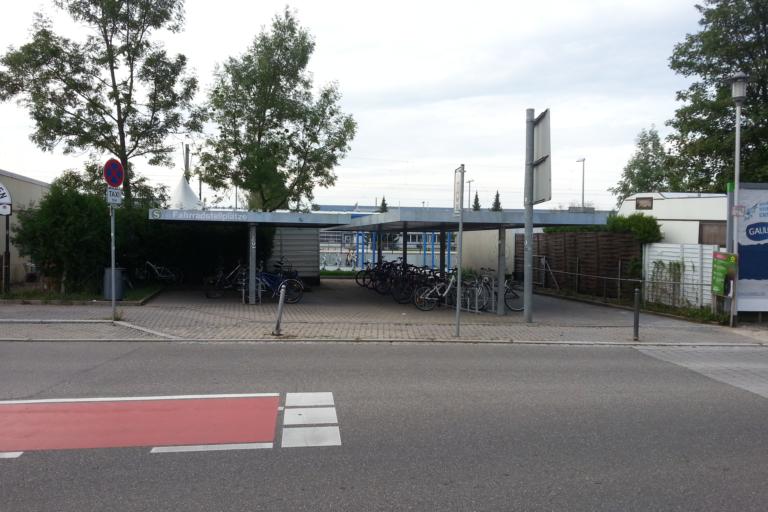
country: DE
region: Baden-Wuerttemberg
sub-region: Regierungsbezirk Stuttgart
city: Renningen
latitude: 48.7748
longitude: 8.9331
